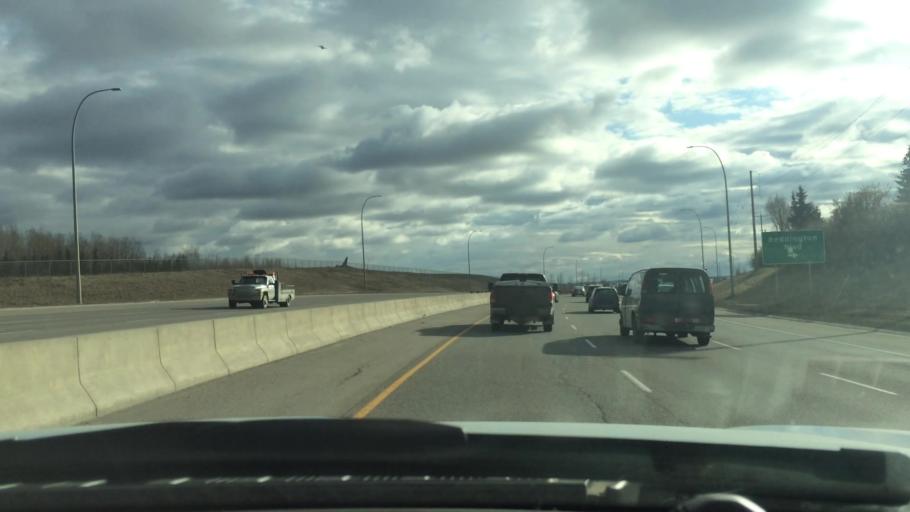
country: CA
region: Alberta
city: Calgary
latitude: 51.1303
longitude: -114.0585
